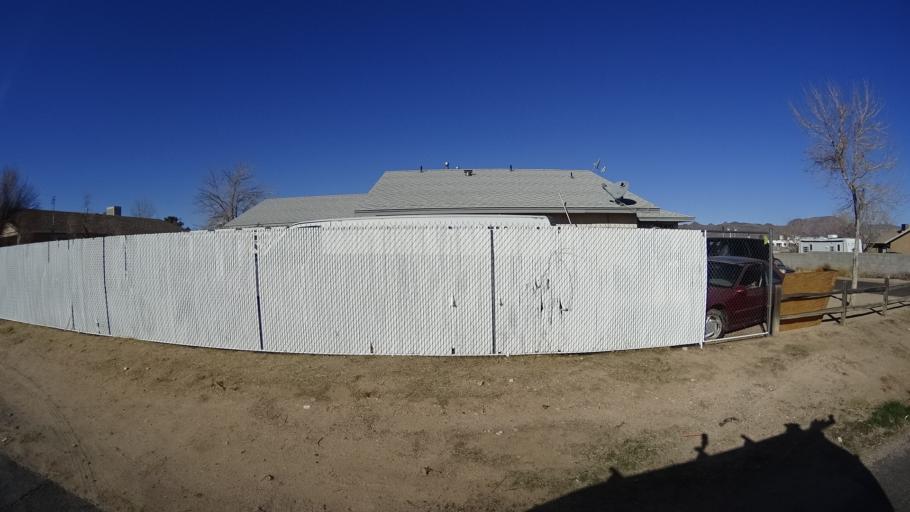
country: US
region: Arizona
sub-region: Mohave County
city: Kingman
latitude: 35.2120
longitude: -114.0103
